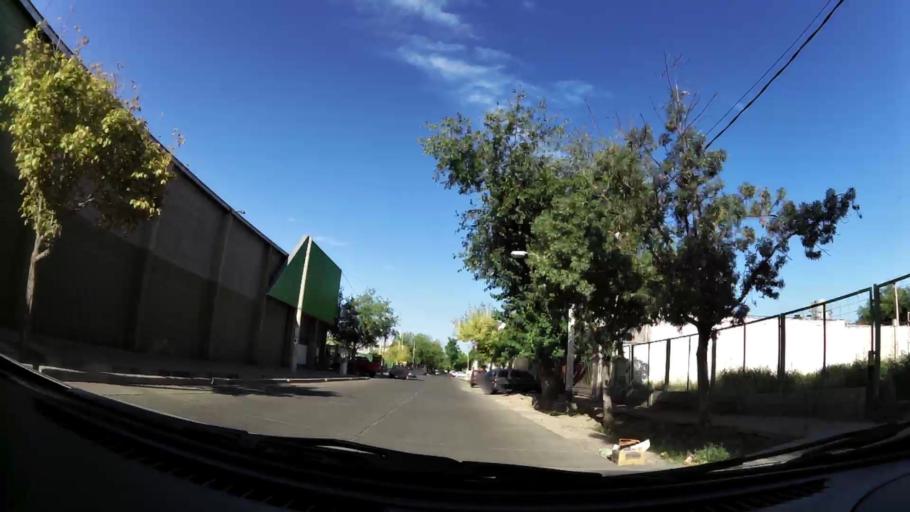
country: AR
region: Mendoza
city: Mendoza
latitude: -32.9031
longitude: -68.8337
